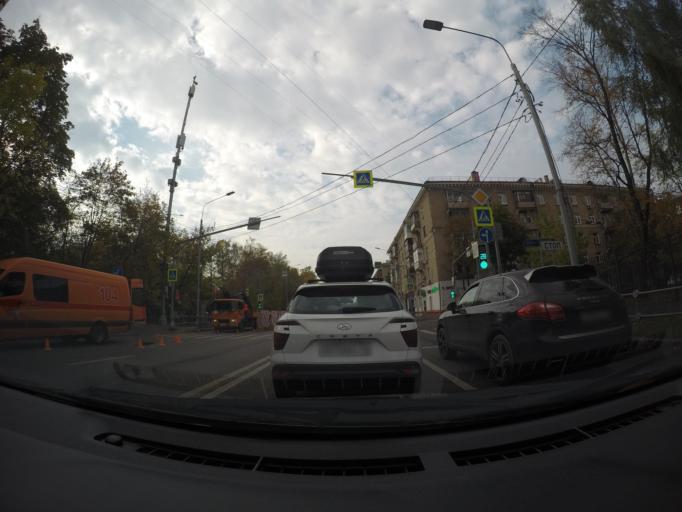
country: RU
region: Moskovskaya
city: Novogireyevo
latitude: 55.7565
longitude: 37.8027
